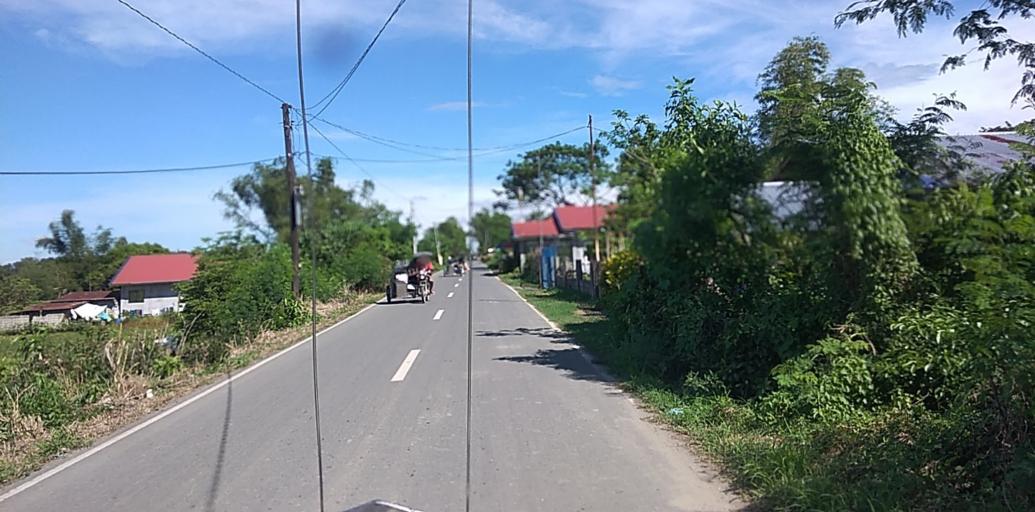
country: PH
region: Central Luzon
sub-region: Province of Pampanga
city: Candaba
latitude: 15.1012
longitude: 120.8145
